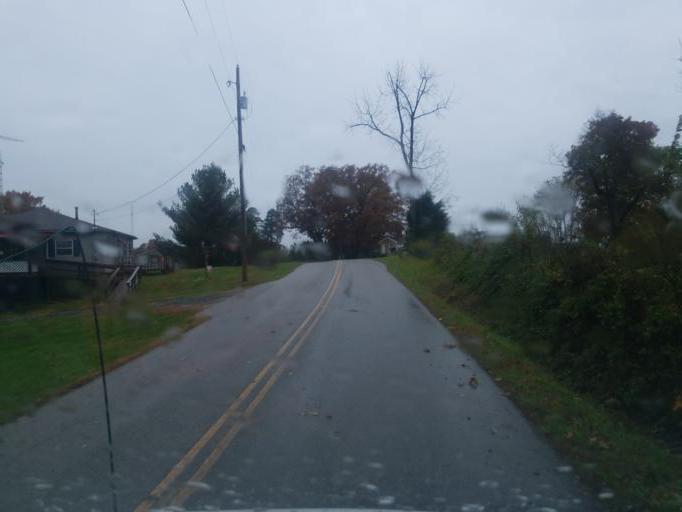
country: US
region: Ohio
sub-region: Washington County
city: Beverly
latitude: 39.4584
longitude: -81.6170
